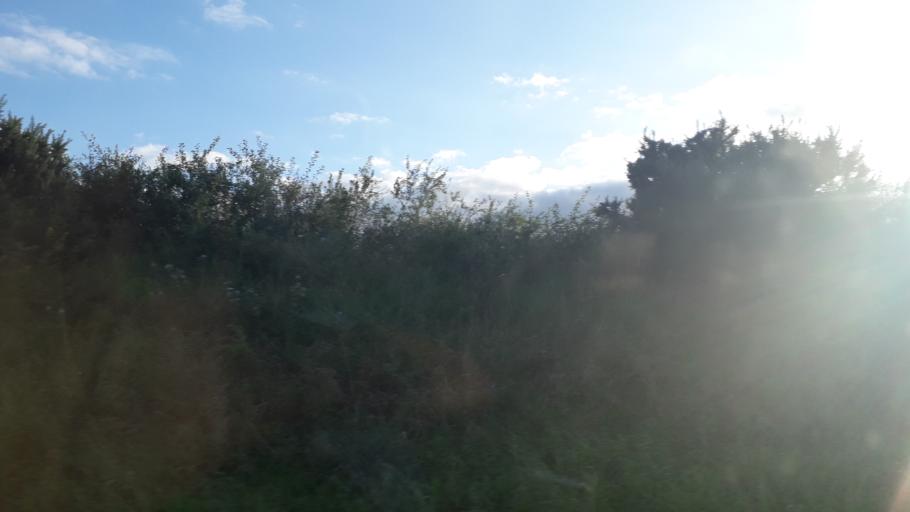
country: IE
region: Leinster
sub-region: Lu
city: Blackrock
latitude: 54.0072
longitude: -6.2899
